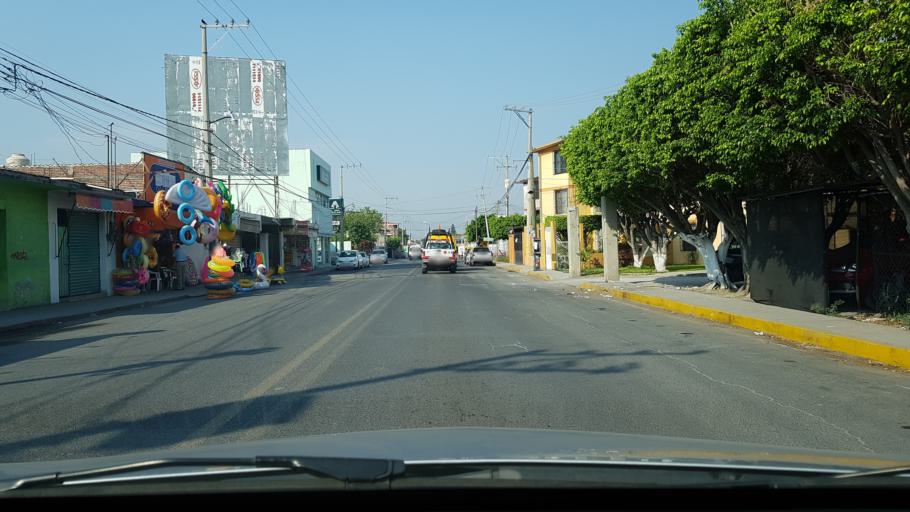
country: MX
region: Morelos
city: Tlaquiltenango
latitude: 18.6269
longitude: -99.1638
